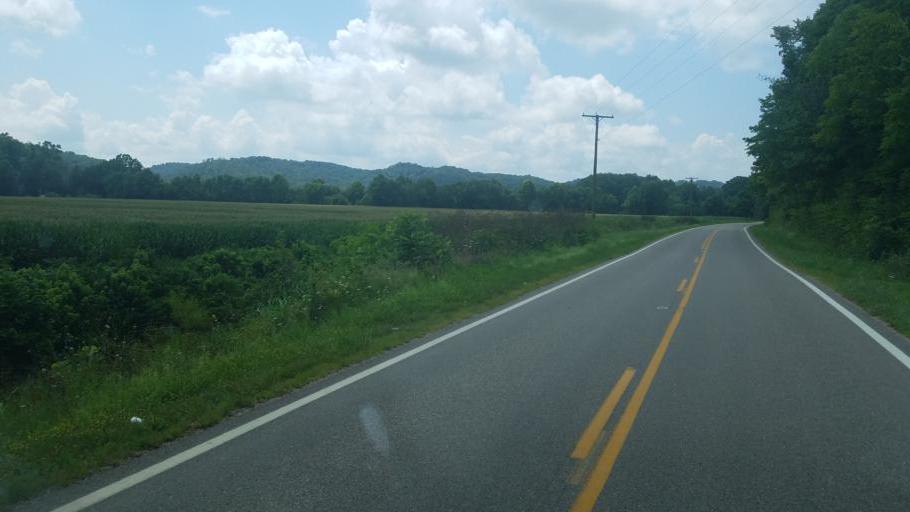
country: US
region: Ohio
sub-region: Ross County
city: Chillicothe
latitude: 39.2980
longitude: -82.7424
